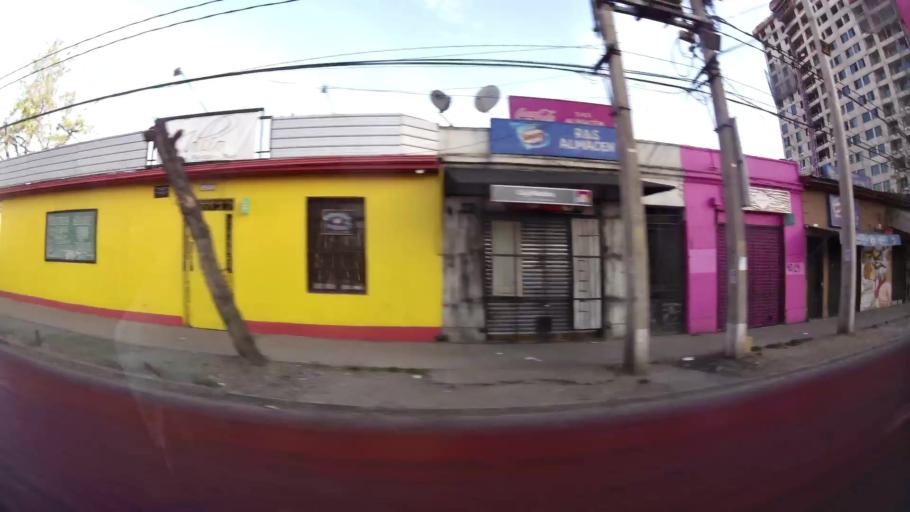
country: CL
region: Santiago Metropolitan
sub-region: Provincia de Santiago
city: Lo Prado
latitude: -33.4377
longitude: -70.6896
